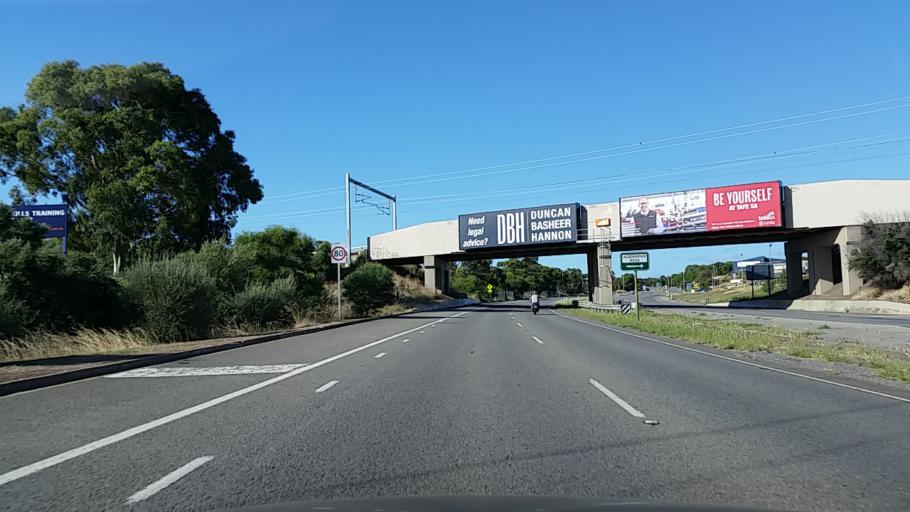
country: AU
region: South Australia
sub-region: Onkaparinga
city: Morphett Vale
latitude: -35.1121
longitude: 138.4925
